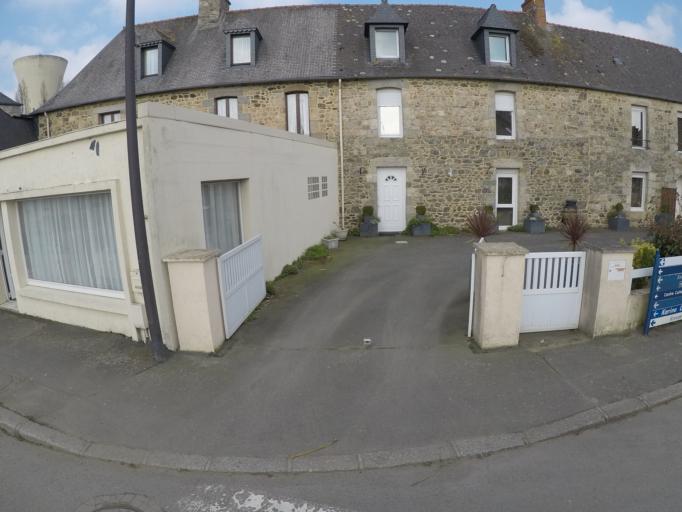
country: FR
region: Brittany
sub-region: Departement des Cotes-d'Armor
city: Pommerit-le-Vicomte
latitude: 48.6204
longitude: -3.0904
